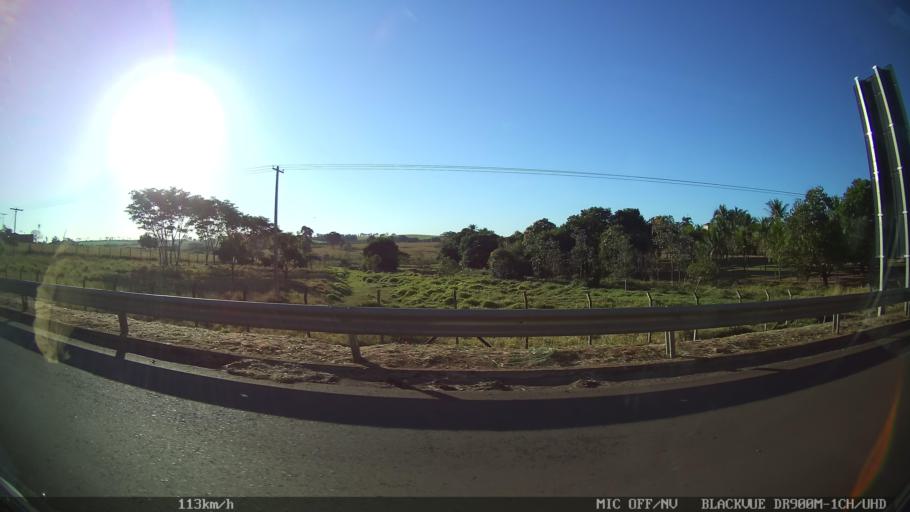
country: BR
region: Sao Paulo
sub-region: Guapiacu
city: Guapiacu
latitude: -20.7876
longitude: -49.2847
